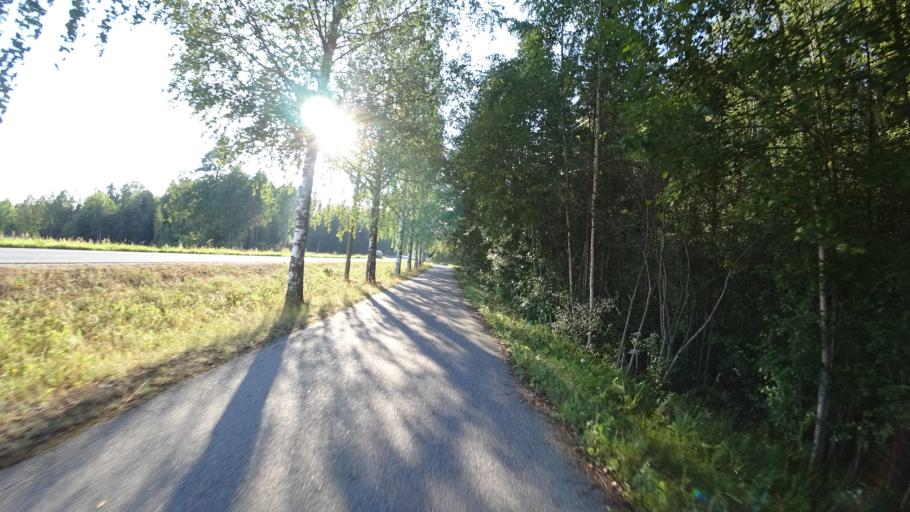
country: FI
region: Pirkanmaa
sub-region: Tampere
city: Nokia
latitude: 61.4699
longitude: 23.3921
